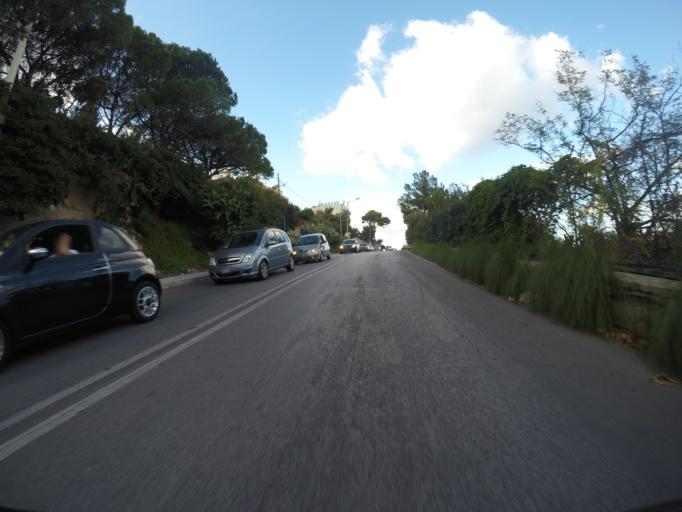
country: IT
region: Sicily
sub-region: Palermo
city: Isola delle Femmine
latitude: 38.2001
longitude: 13.2690
